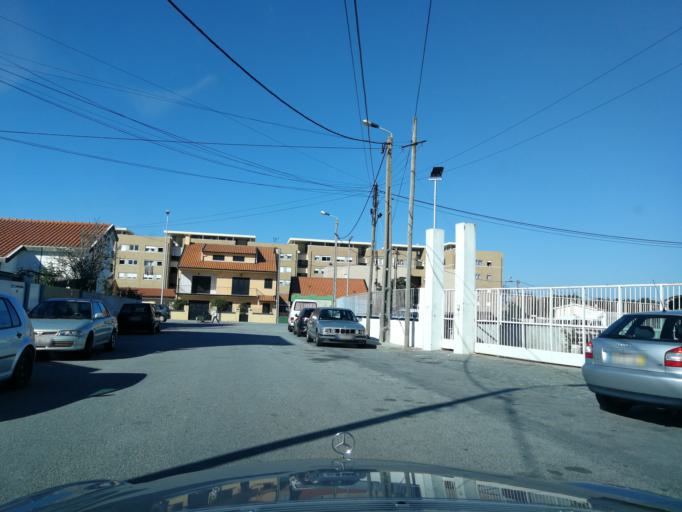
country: PT
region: Porto
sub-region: Vila do Conde
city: Vila do Conde
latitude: 41.3648
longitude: -8.7443
